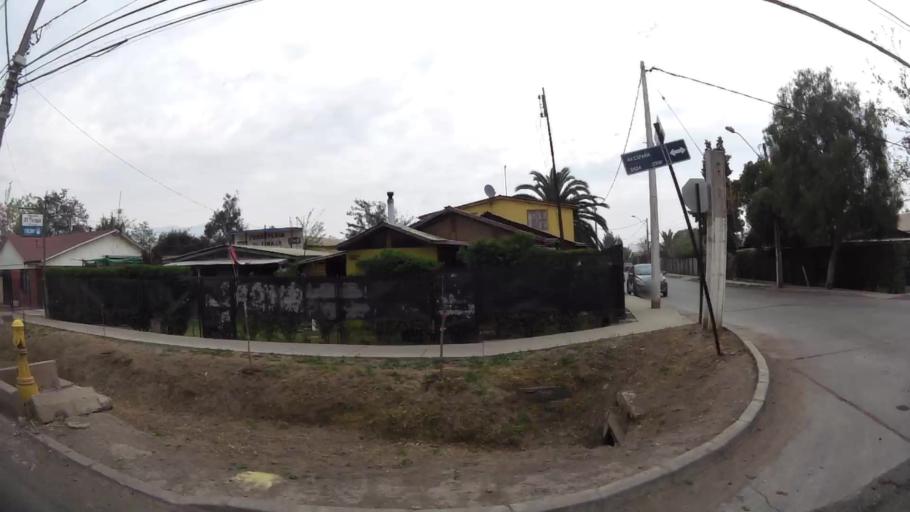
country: CL
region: Santiago Metropolitan
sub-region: Provincia de Chacabuco
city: Lampa
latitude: -33.2379
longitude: -70.8079
